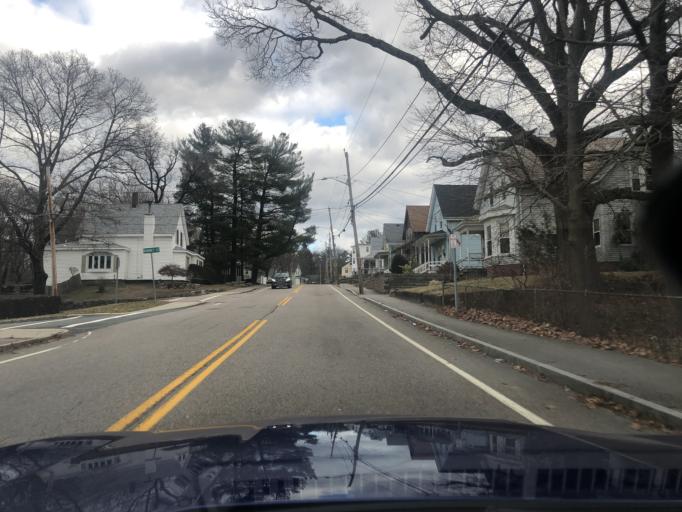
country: US
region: Massachusetts
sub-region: Plymouth County
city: Brockton
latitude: 42.1099
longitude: -71.0167
